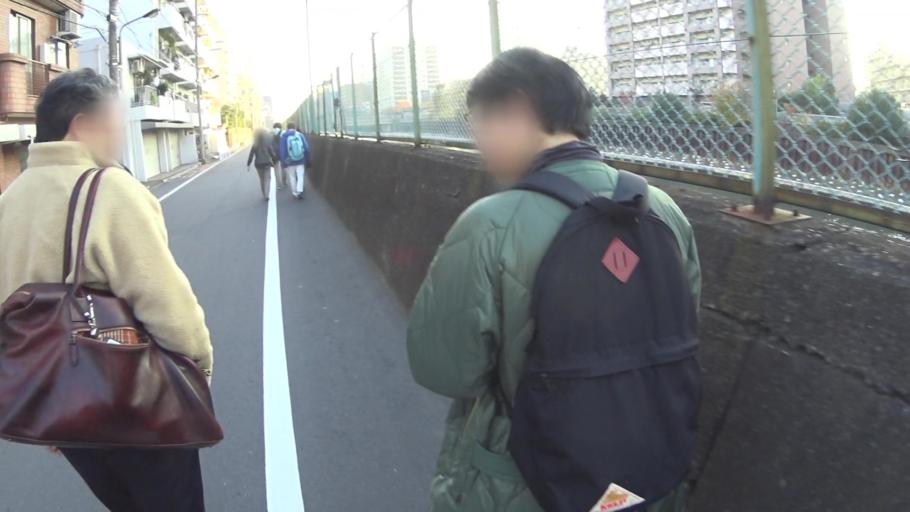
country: JP
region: Tokyo
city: Urayasu
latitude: 35.7064
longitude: 139.8187
